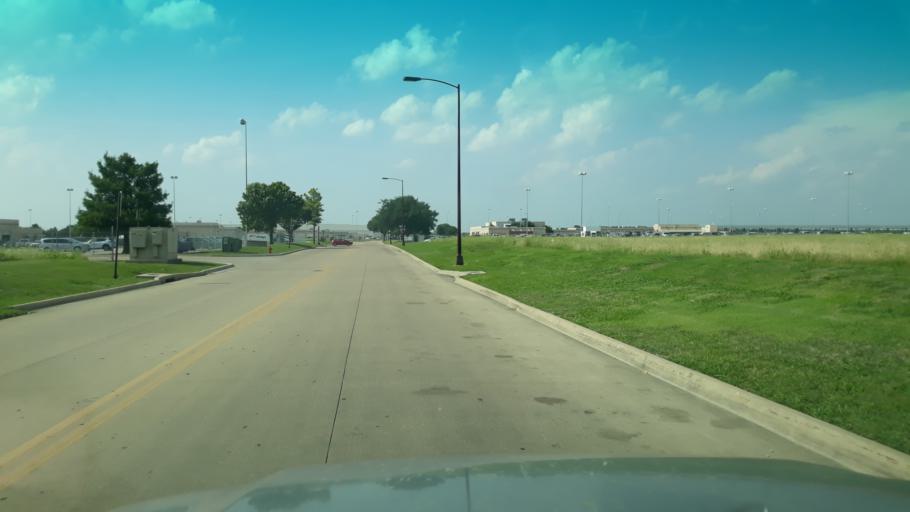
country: US
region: Texas
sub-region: Tarrant County
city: Euless
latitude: 32.8545
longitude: -97.0286
